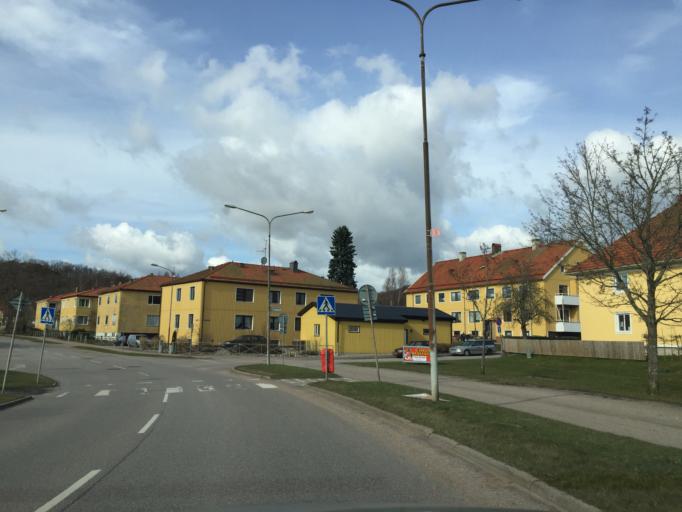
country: SE
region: Vaestra Goetaland
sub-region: Uddevalla Kommun
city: Uddevalla
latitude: 58.3548
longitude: 11.9450
